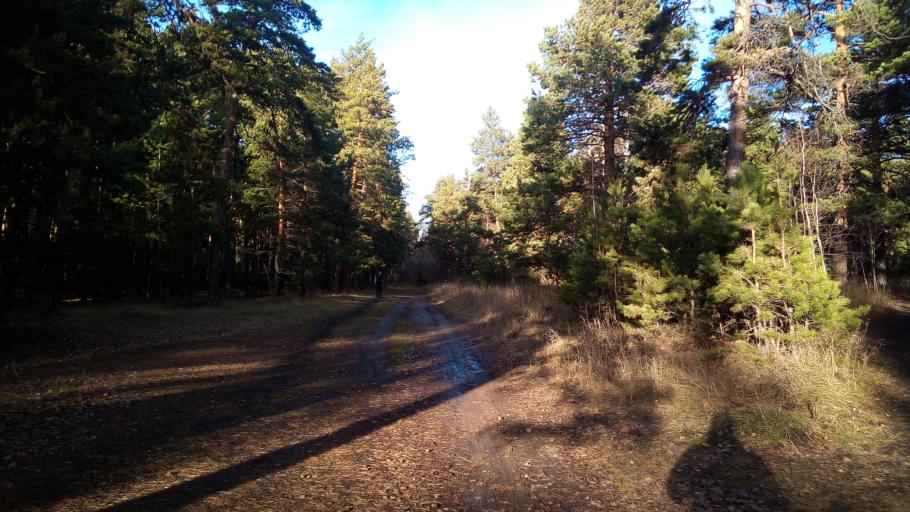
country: RU
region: Chelyabinsk
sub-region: Gorod Chelyabinsk
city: Chelyabinsk
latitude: 55.1564
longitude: 61.3521
